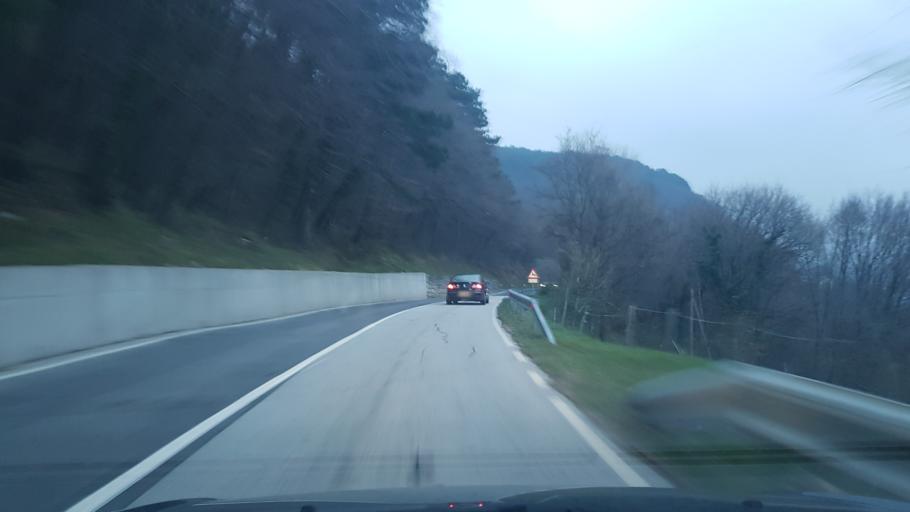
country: SI
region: Vipava
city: Vipava
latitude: 45.8827
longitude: 13.9822
